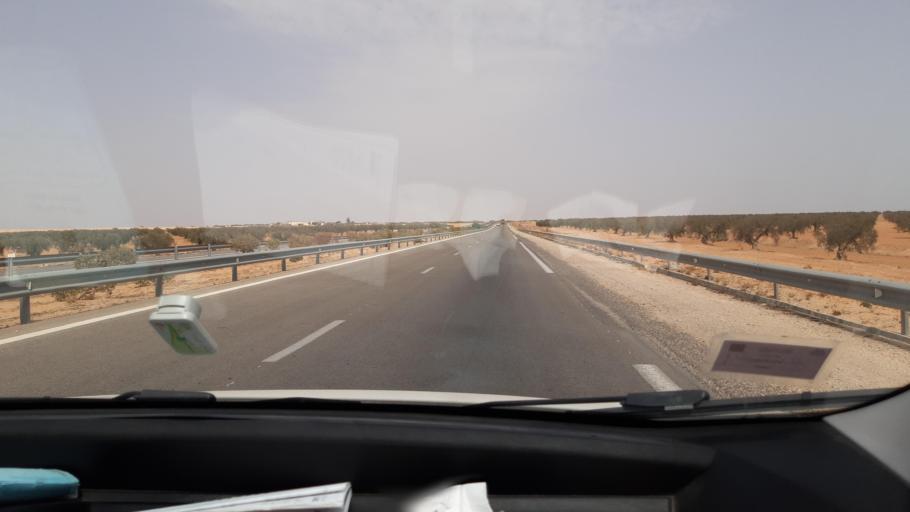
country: TN
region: Safaqis
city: Bi'r `Ali Bin Khalifah
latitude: 34.5593
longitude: 10.3375
